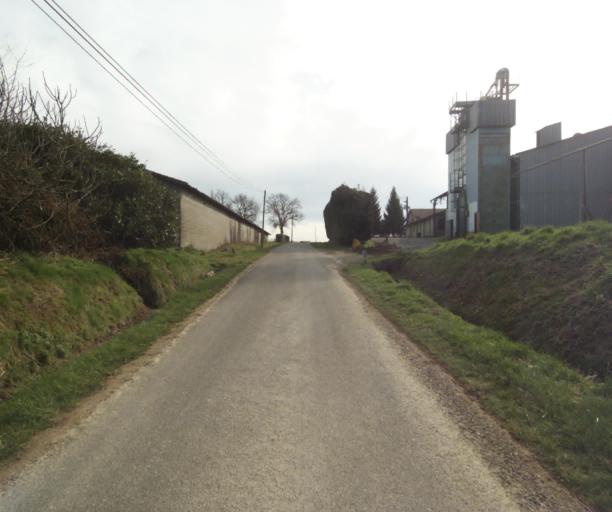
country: FR
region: Aquitaine
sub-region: Departement des Landes
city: Gabarret
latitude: 43.9370
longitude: 0.0450
